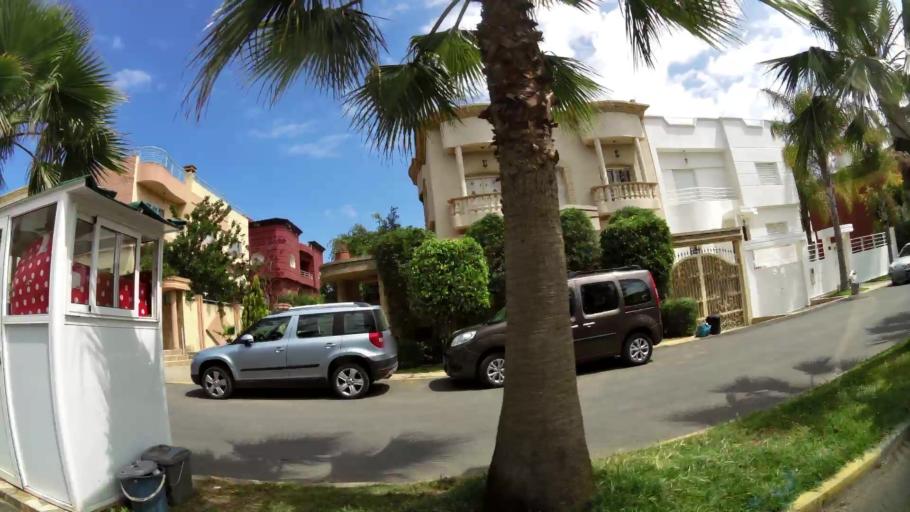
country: MA
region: Gharb-Chrarda-Beni Hssen
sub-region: Kenitra Province
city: Kenitra
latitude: 34.2428
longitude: -6.6041
